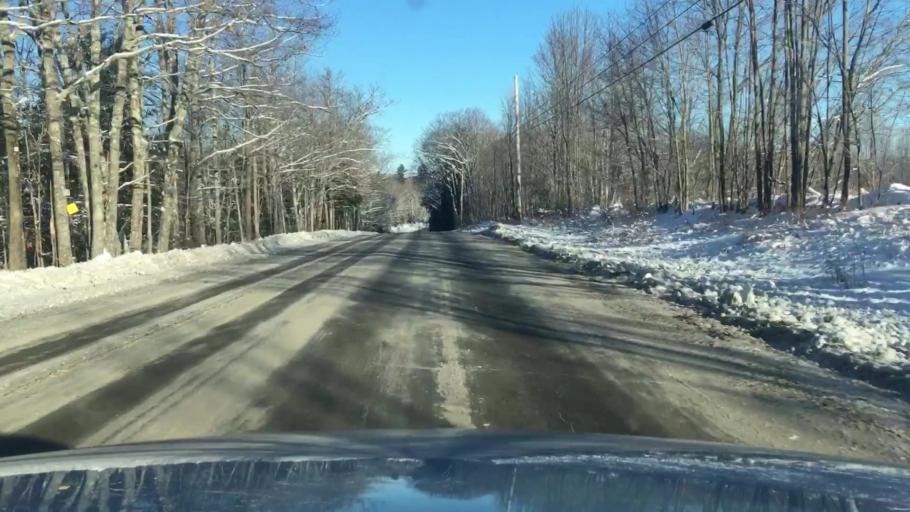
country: US
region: Maine
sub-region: Kennebec County
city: Mount Vernon
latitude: 44.4656
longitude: -69.9736
